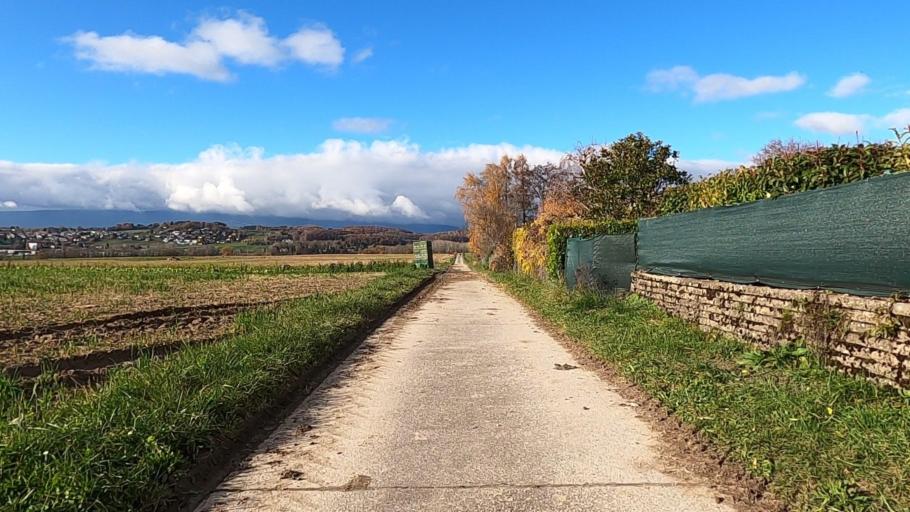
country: CH
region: Vaud
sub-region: Morges District
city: Saint-Prex
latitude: 46.5152
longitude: 6.4478
